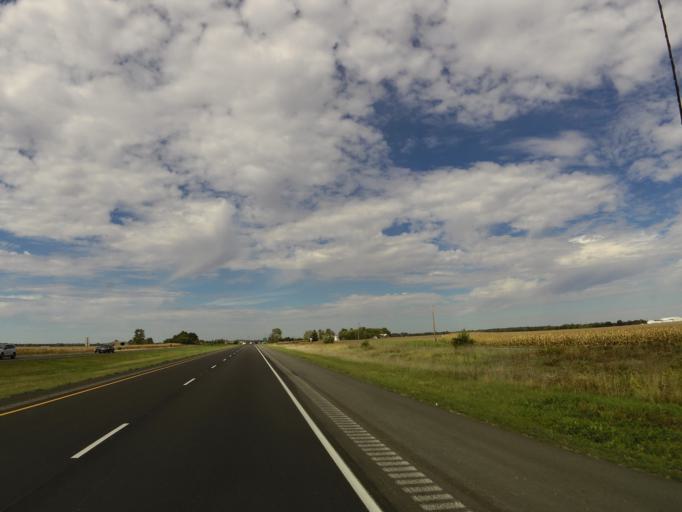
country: US
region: Illinois
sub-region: McLean County
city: Le Roy
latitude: 40.3039
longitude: -88.7164
